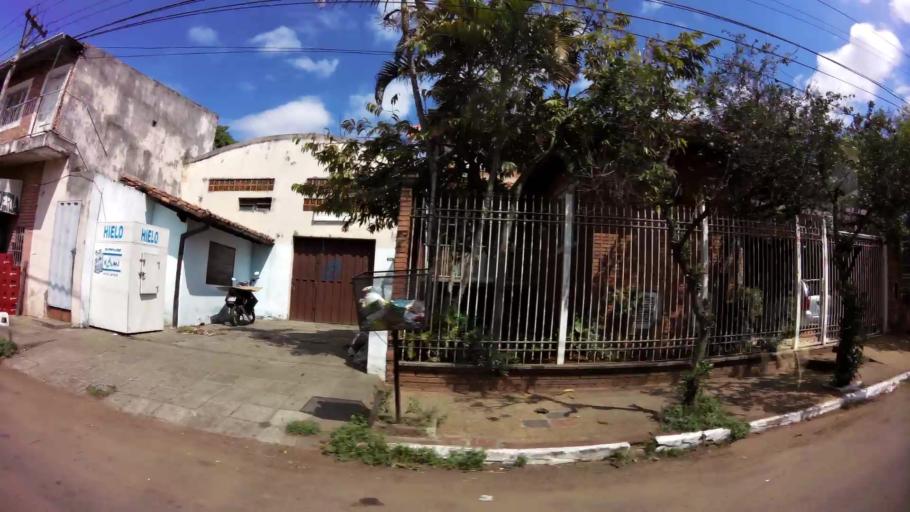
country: PY
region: Central
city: San Lorenzo
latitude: -25.3432
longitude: -57.5136
